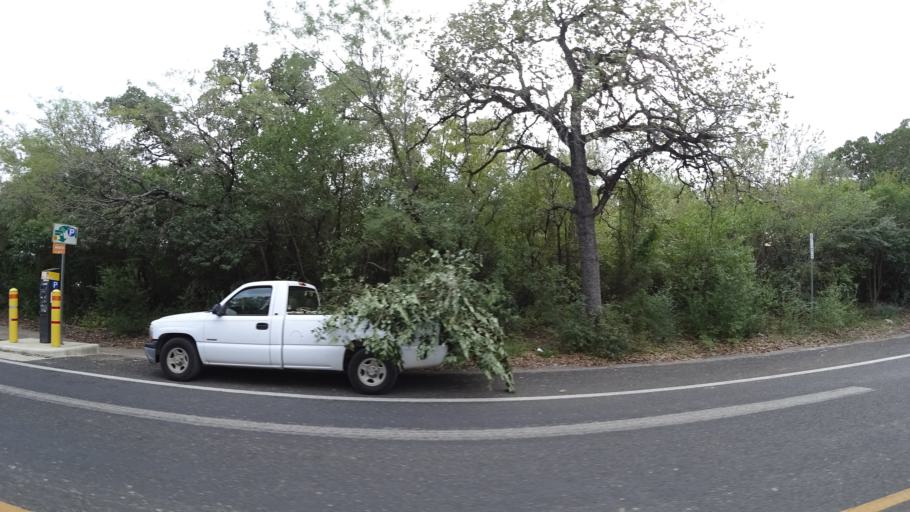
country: US
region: Texas
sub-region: Travis County
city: West Lake Hills
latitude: 30.2952
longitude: -97.7818
